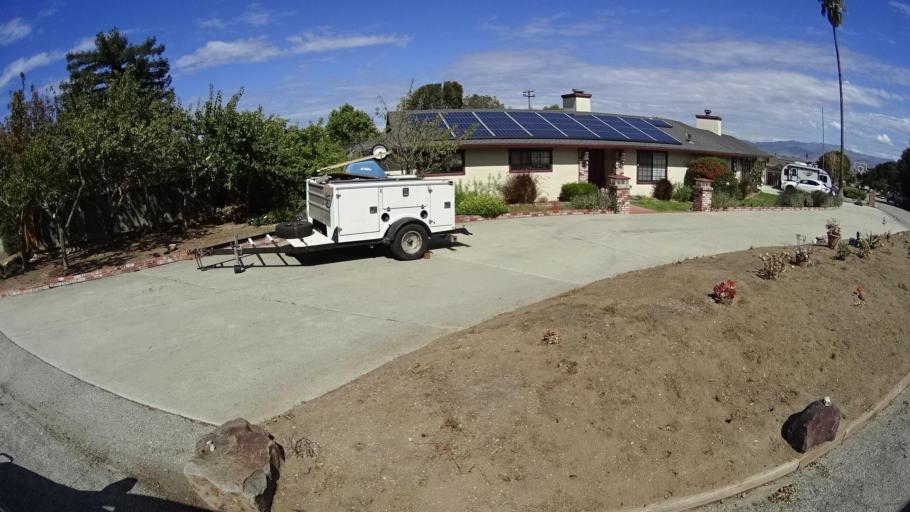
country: US
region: California
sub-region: Monterey County
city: Salinas
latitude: 36.5949
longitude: -121.6326
